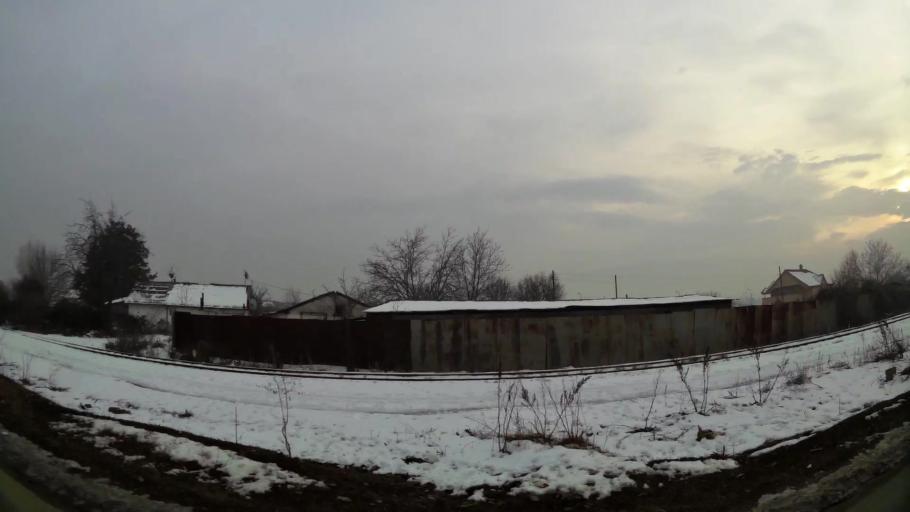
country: MK
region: Suto Orizari
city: Suto Orizare
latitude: 42.0279
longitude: 21.4182
